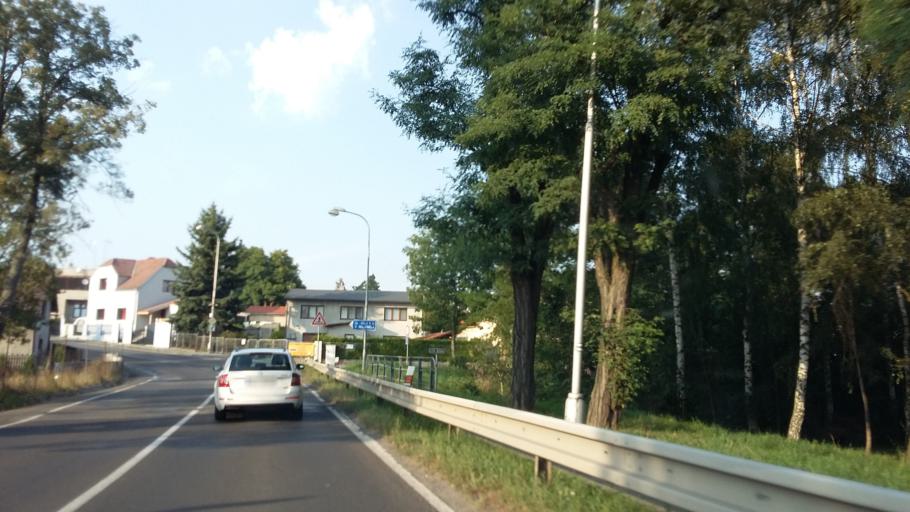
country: CZ
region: Central Bohemia
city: Bakov nad Jizerou
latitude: 50.4700
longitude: 14.9428
